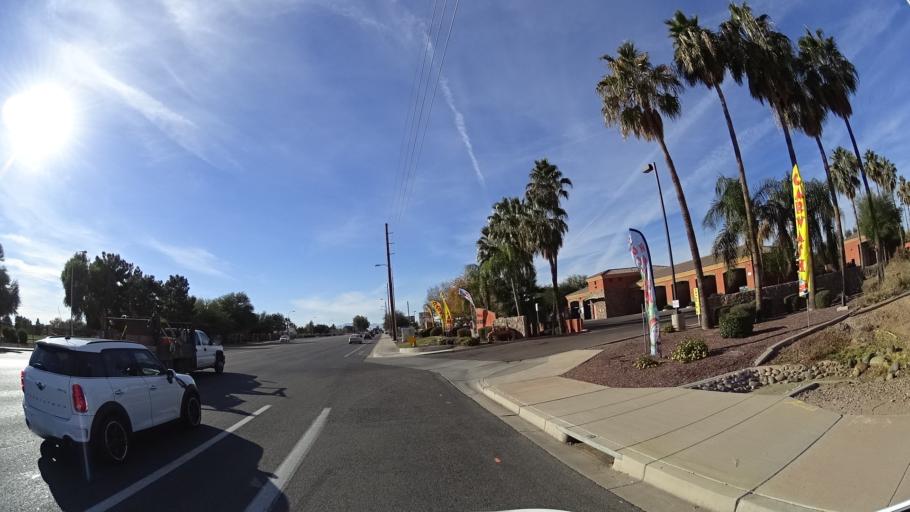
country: US
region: Arizona
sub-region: Maricopa County
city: Sun Lakes
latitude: 33.2190
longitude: -111.8178
